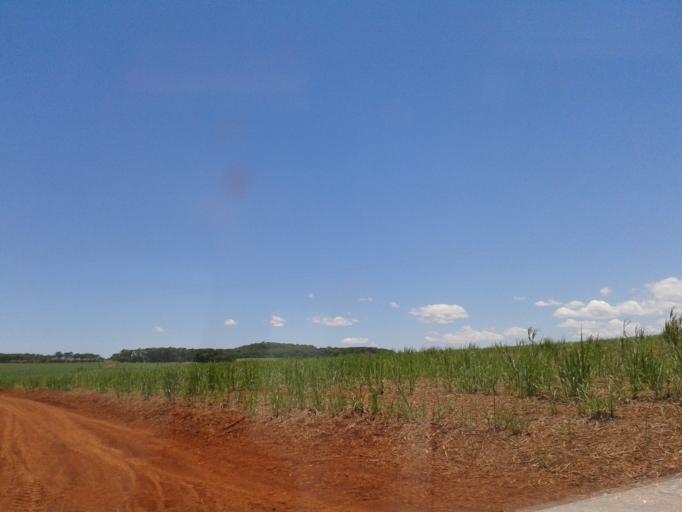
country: BR
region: Minas Gerais
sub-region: Centralina
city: Centralina
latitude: -18.6660
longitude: -49.2357
